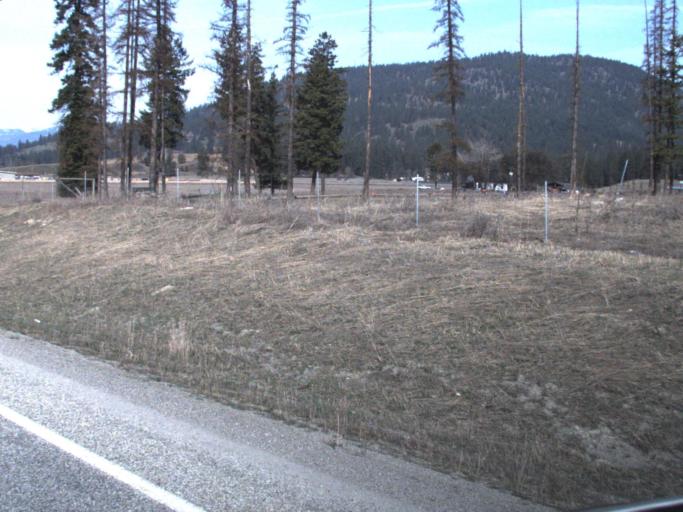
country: US
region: Washington
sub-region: Stevens County
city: Colville
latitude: 48.5475
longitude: -117.8628
